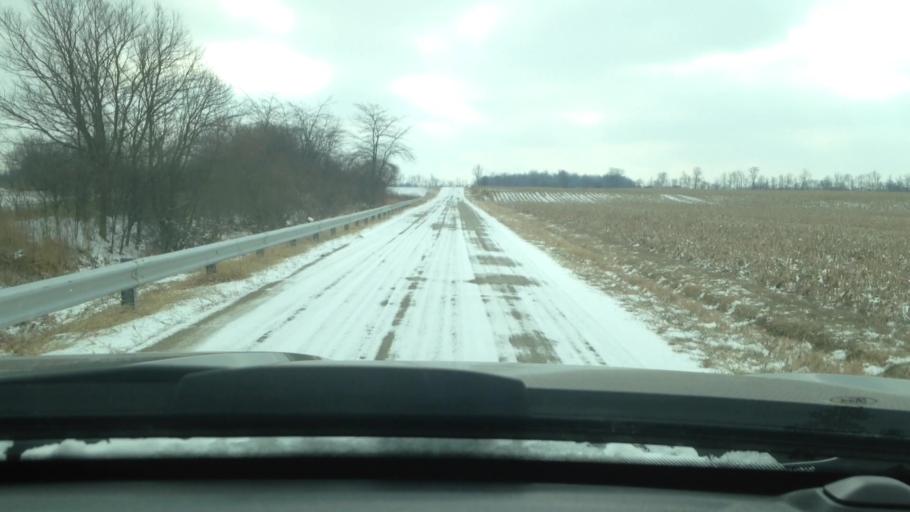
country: US
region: Indiana
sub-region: Randolph County
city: Union City
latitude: 40.2648
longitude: -84.8622
